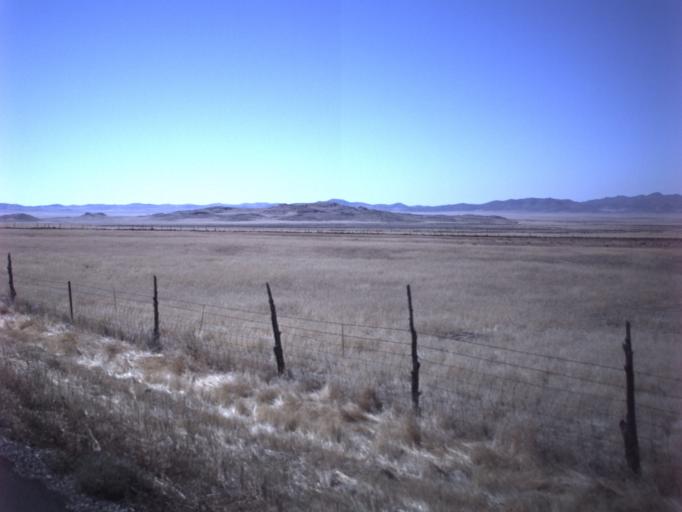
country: US
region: Utah
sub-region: Tooele County
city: Grantsville
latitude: 40.4214
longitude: -112.7488
